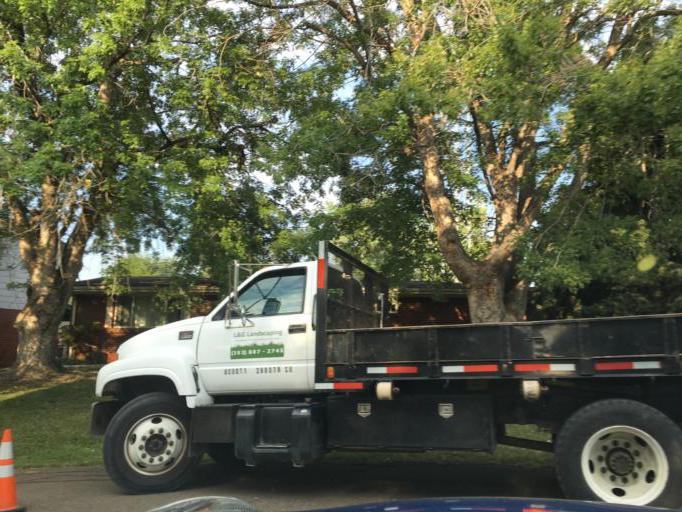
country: US
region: Colorado
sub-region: Jefferson County
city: Wheat Ridge
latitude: 39.7464
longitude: -105.1059
